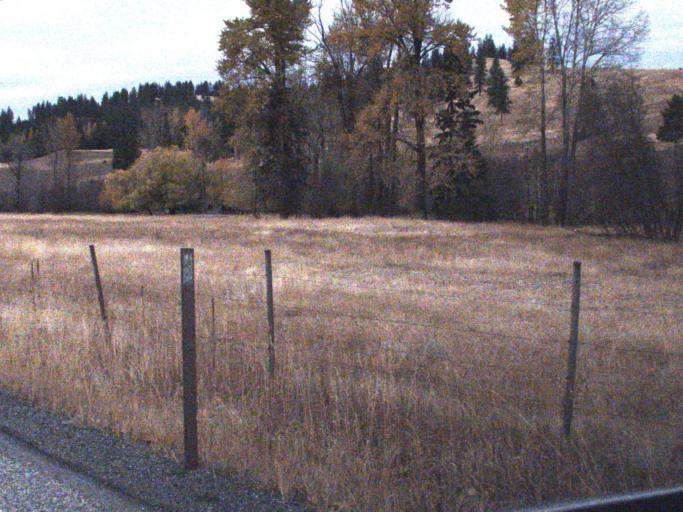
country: US
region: Washington
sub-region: Ferry County
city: Republic
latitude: 48.6043
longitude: -118.6565
